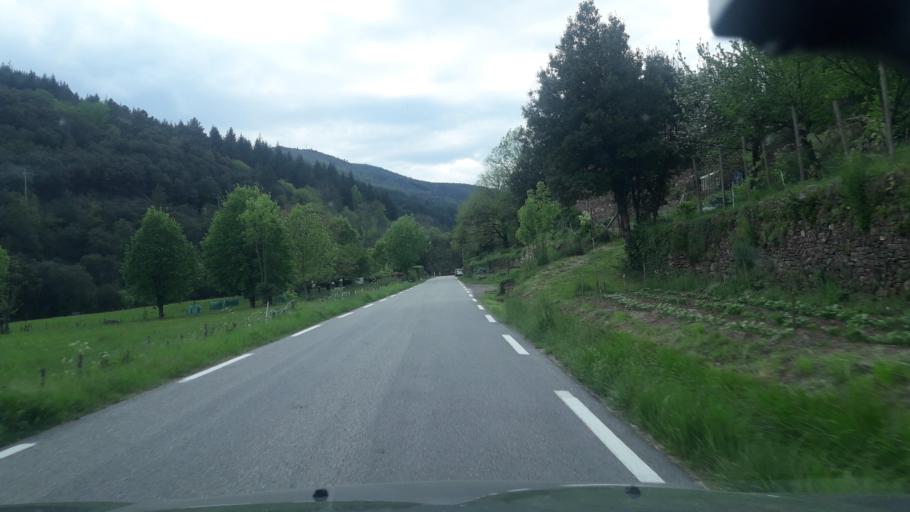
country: FR
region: Languedoc-Roussillon
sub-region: Departement du Gard
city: Valleraugue
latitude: 44.1402
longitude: 3.7292
